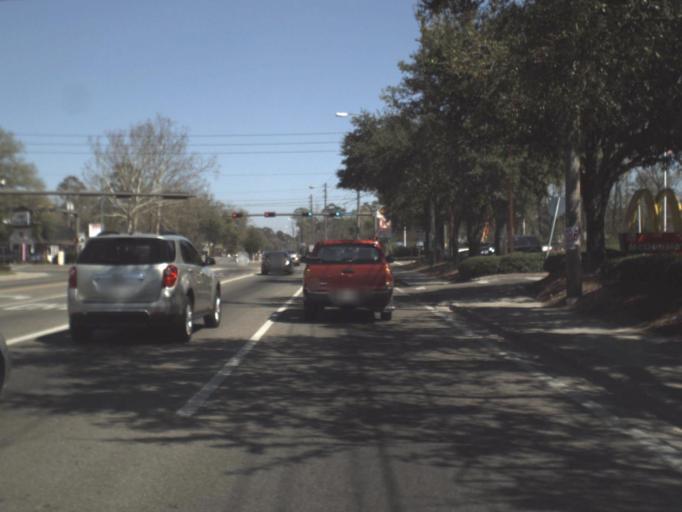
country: US
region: Florida
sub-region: Leon County
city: Tallahassee
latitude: 30.4125
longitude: -84.2816
